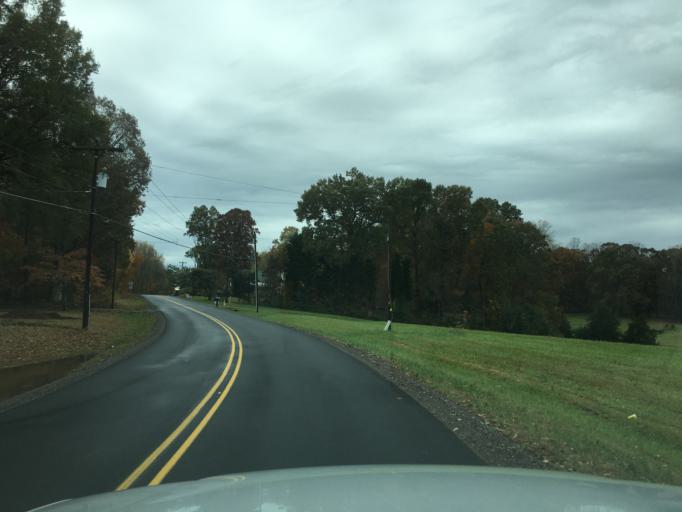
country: US
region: North Carolina
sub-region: Catawba County
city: Newton
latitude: 35.6267
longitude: -81.2230
